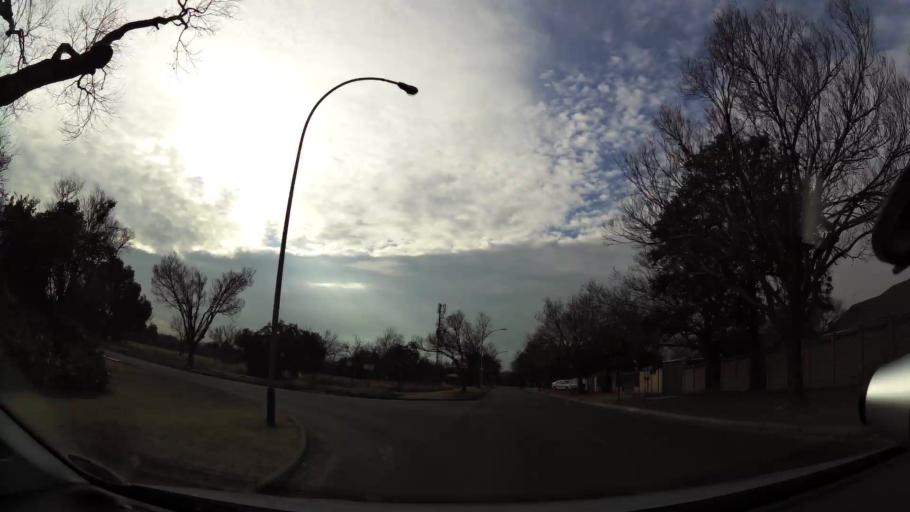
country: ZA
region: Orange Free State
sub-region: Mangaung Metropolitan Municipality
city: Bloemfontein
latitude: -29.1222
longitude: 26.1851
